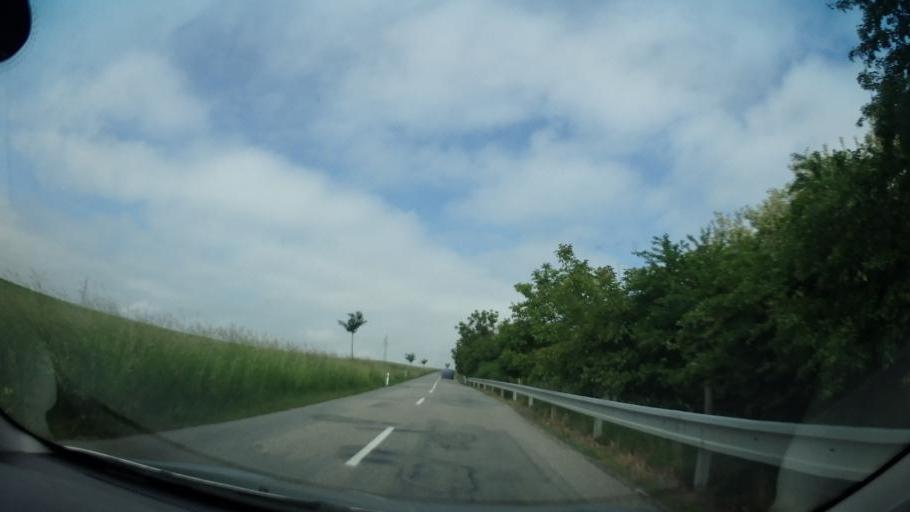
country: CZ
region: South Moravian
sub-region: Okres Brno-Venkov
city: Dolni Loucky
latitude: 49.3790
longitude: 16.3489
